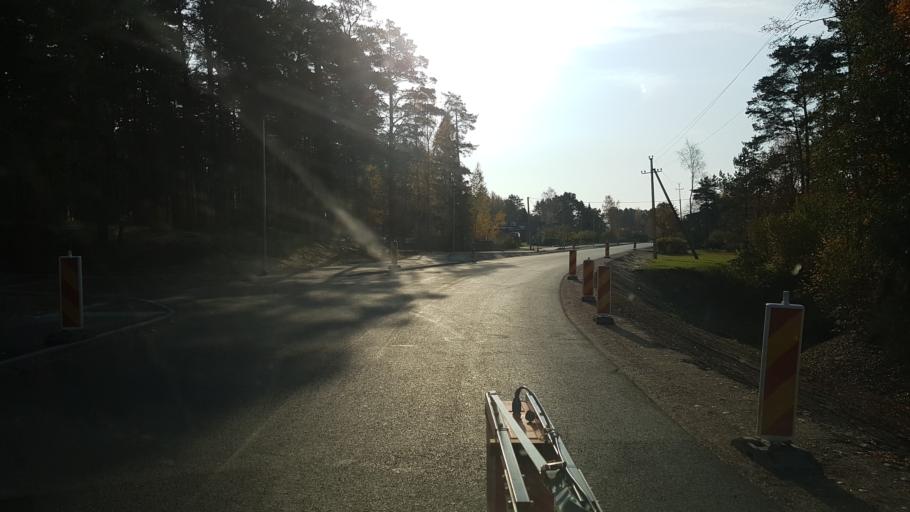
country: EE
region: Paernumaa
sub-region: Paikuse vald
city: Paikuse
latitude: 58.3544
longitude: 24.6184
